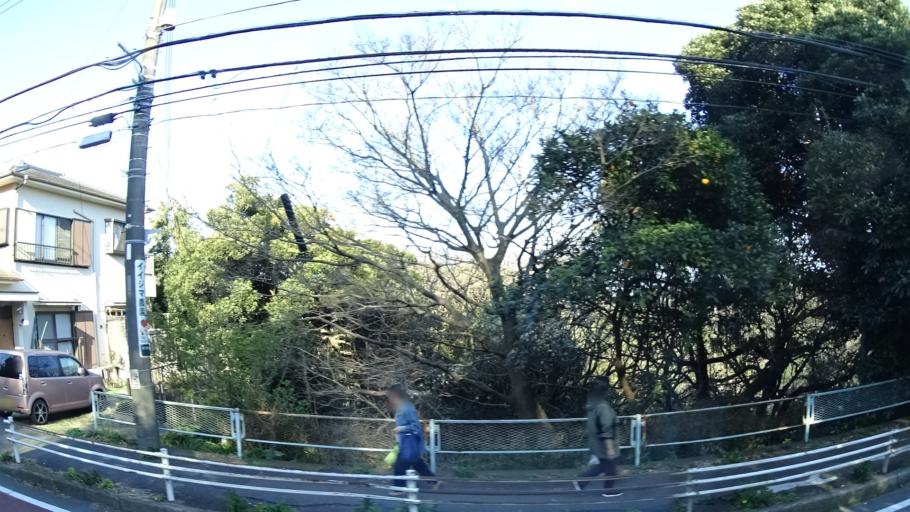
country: JP
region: Kanagawa
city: Miura
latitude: 35.1619
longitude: 139.6412
